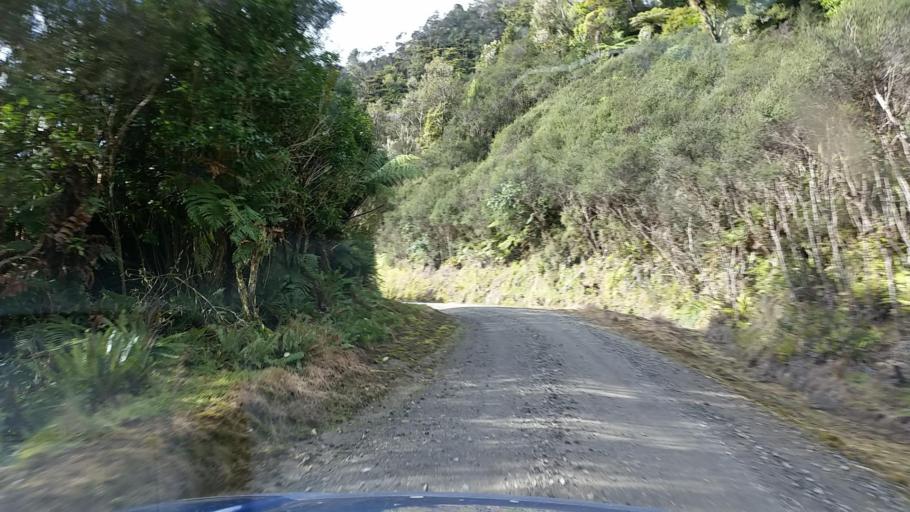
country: NZ
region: Taranaki
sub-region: South Taranaki District
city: Eltham
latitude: -39.2798
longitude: 174.7575
